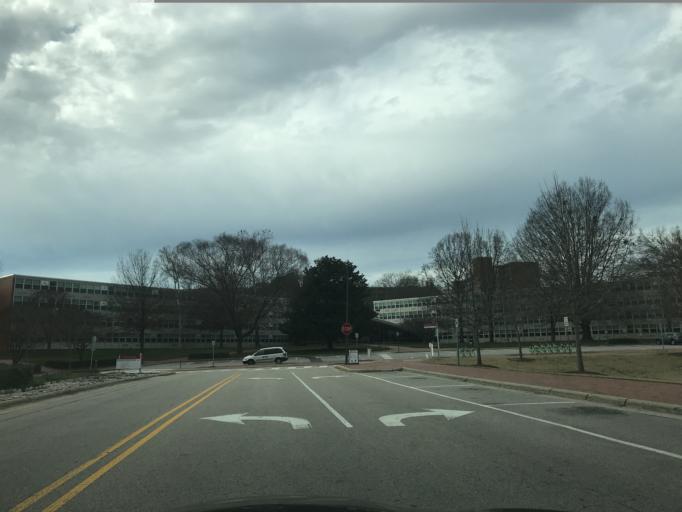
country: US
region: North Carolina
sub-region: Wake County
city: West Raleigh
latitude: 35.7850
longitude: -78.6751
